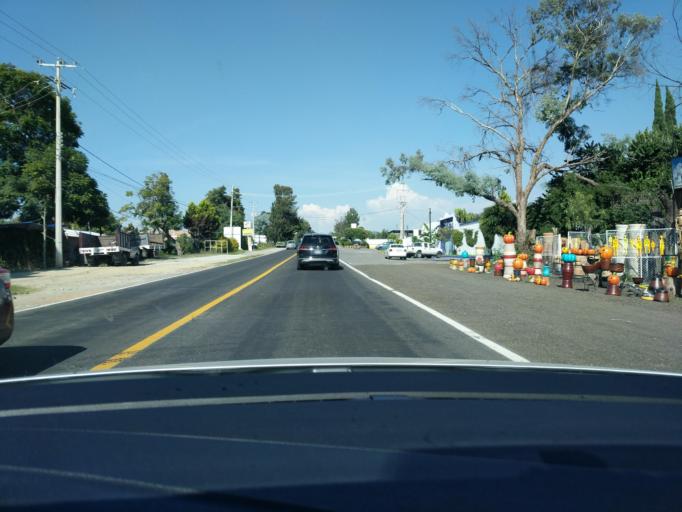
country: MX
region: Puebla
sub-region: Santa Isabel Cholula
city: Santa Ana Acozautla
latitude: 18.9403
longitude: -98.3987
